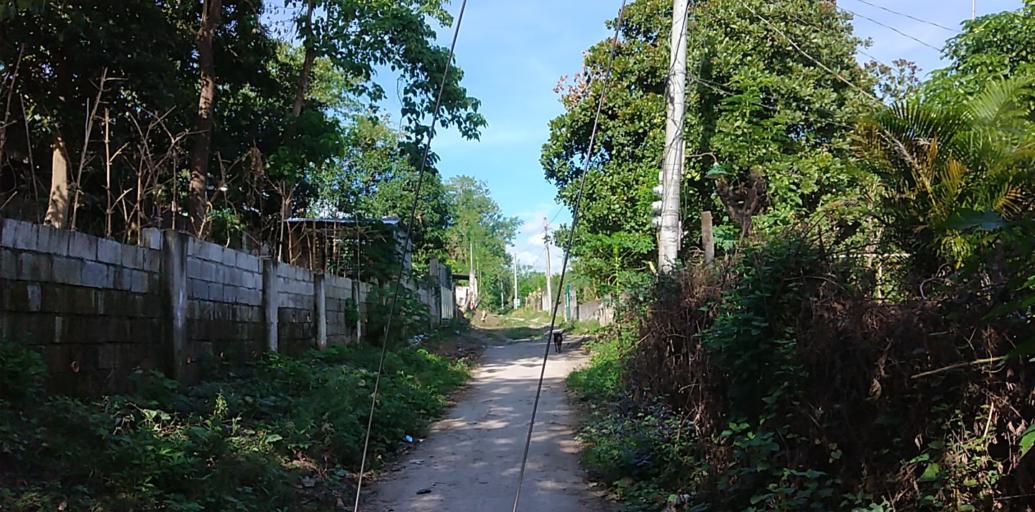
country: PH
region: Central Luzon
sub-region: Province of Pampanga
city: Porac
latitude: 15.0789
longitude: 120.5384
